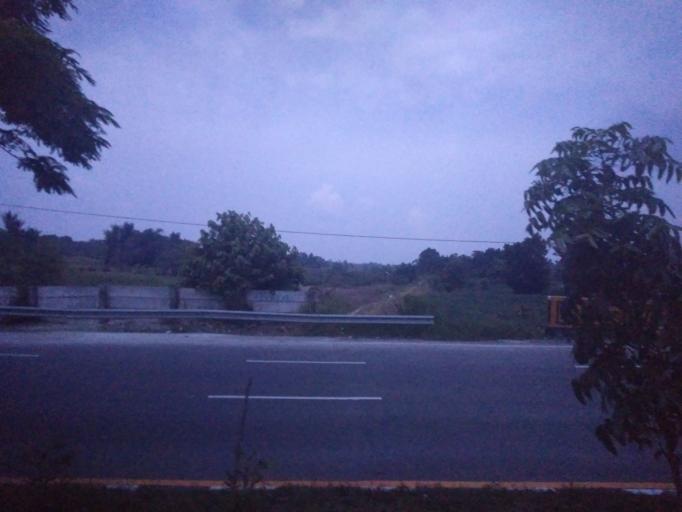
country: ID
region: North Sumatra
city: Percut
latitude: 3.6024
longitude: 98.8464
